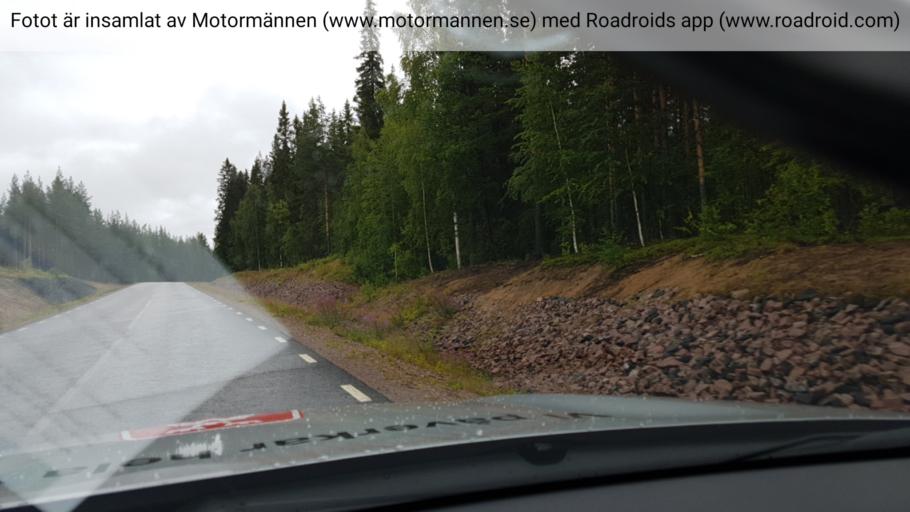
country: SE
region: Norrbotten
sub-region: Gallivare Kommun
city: Gaellivare
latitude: 66.6454
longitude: 20.3922
